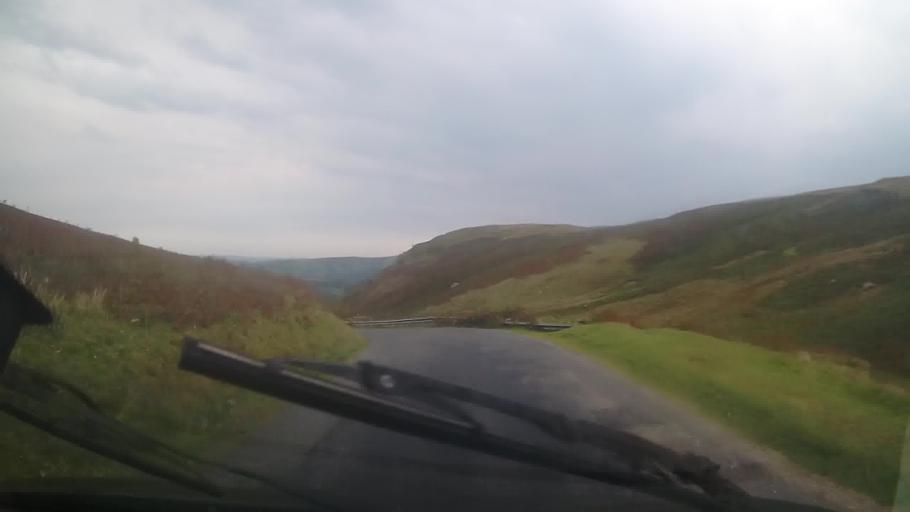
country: GB
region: Wales
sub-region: Sir Powys
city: Rhayader
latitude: 52.3157
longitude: -3.5668
